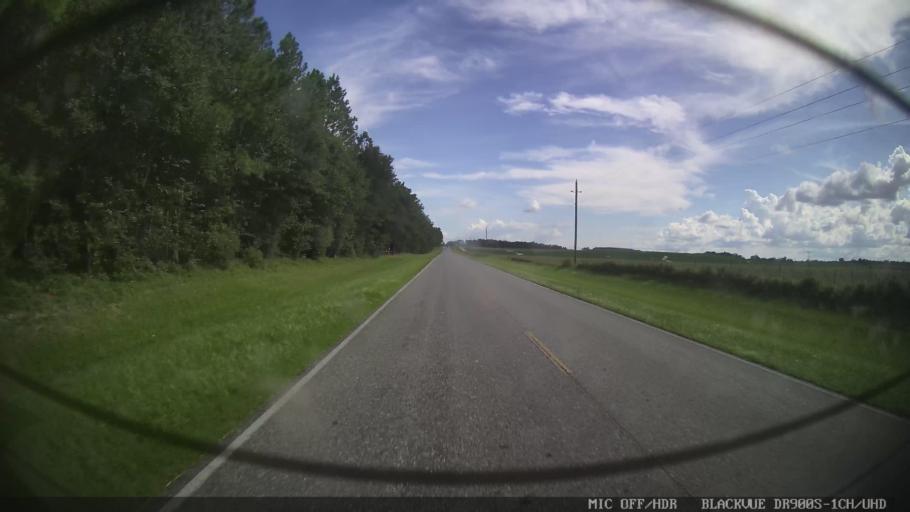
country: US
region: Georgia
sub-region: Echols County
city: Statenville
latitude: 30.5929
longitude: -83.2242
